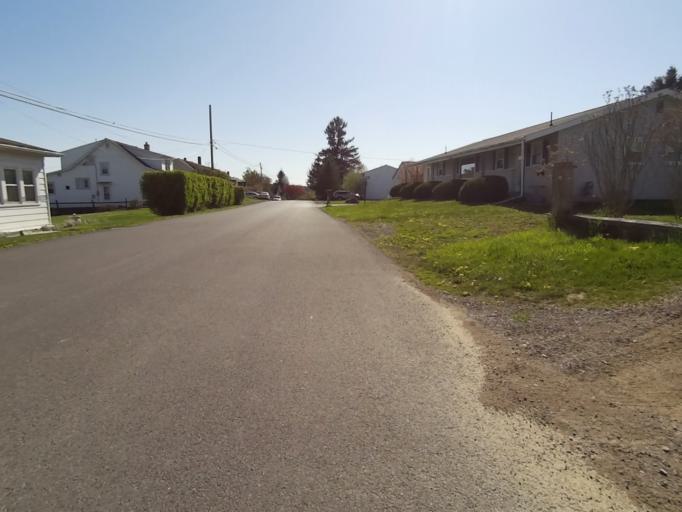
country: US
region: Pennsylvania
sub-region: Centre County
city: Bellefonte
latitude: 40.9090
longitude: -77.7878
